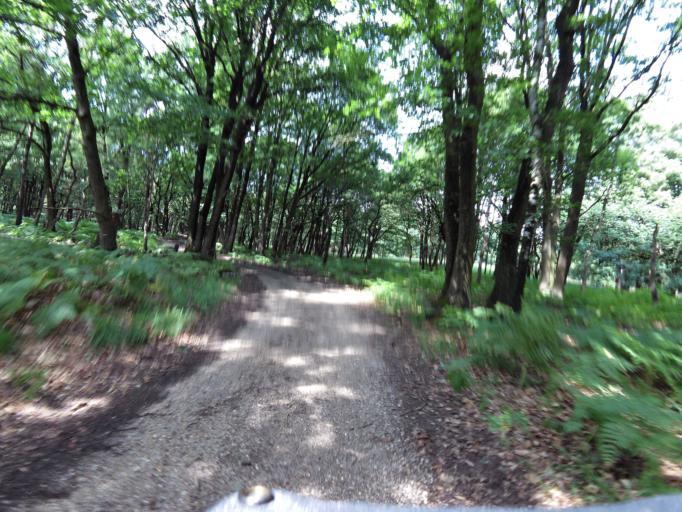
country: DE
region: North Rhine-Westphalia
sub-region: Regierungsbezirk Koln
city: Wassenberg
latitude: 51.1632
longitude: 6.1420
